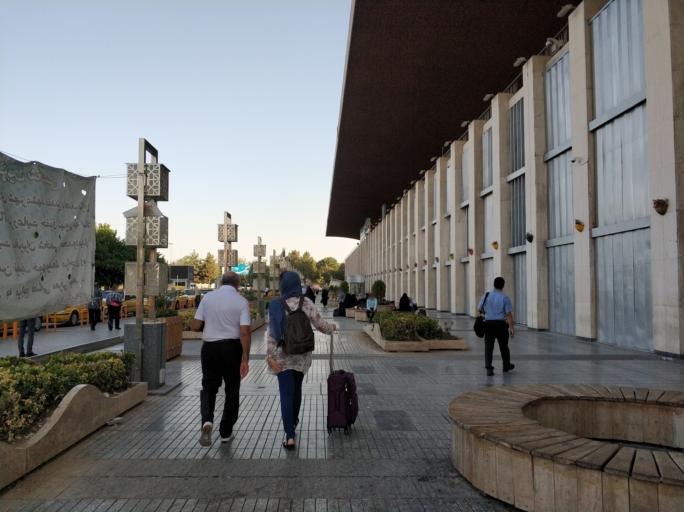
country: IR
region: Razavi Khorasan
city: Mashhad
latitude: 36.3037
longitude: 59.6239
